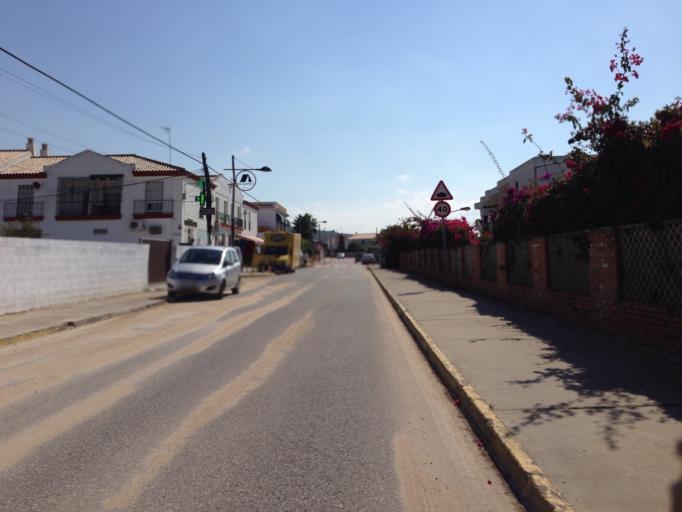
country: ES
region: Andalusia
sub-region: Provincia de Cadiz
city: Vejer de la Frontera
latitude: 36.1863
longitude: -6.0155
